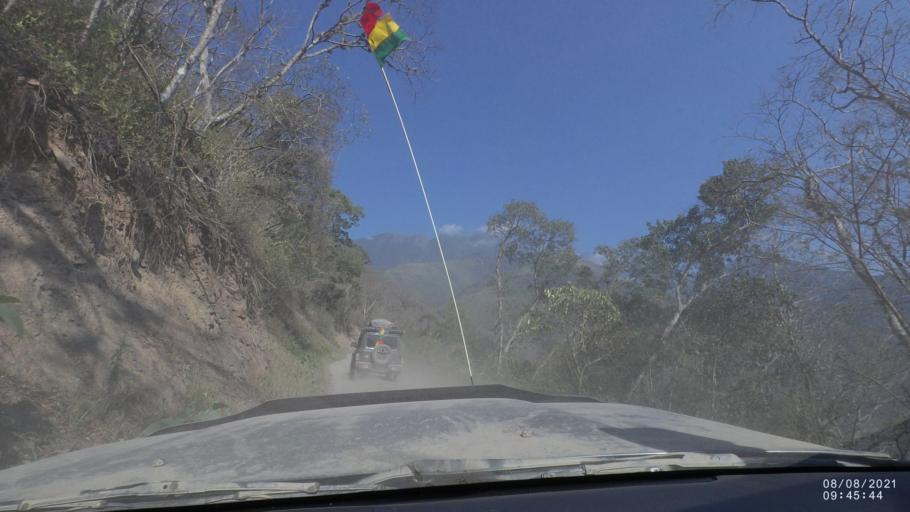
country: BO
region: La Paz
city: Quime
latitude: -16.6047
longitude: -66.7273
